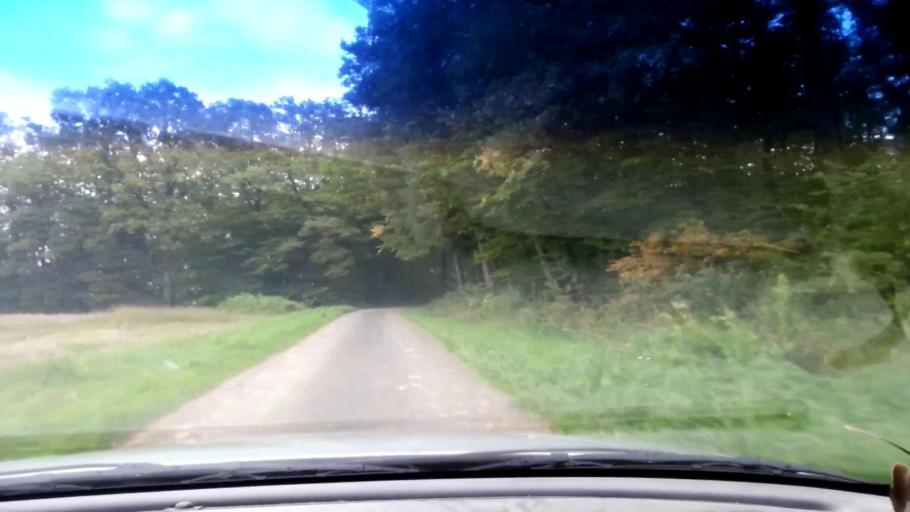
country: DE
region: Bavaria
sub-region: Upper Franconia
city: Memmelsdorf
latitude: 49.9694
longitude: 10.9542
